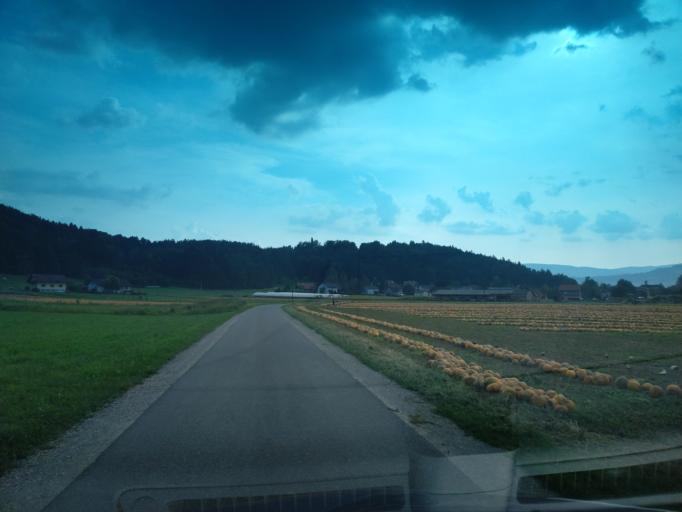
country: AT
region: Styria
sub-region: Politischer Bezirk Deutschlandsberg
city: Wies
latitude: 46.7193
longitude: 15.2796
